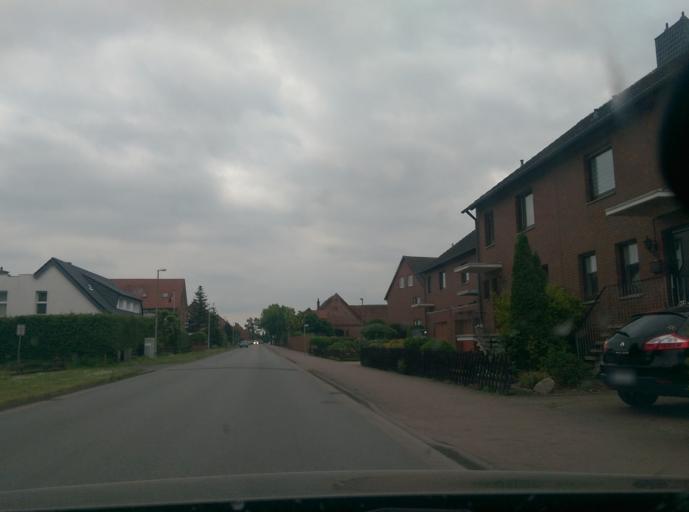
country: DE
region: Lower Saxony
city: Garbsen-Mitte
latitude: 52.4611
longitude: 9.6034
